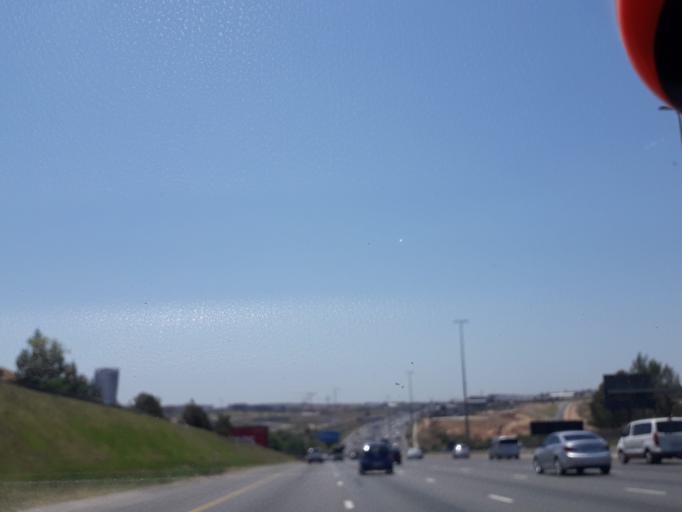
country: ZA
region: Gauteng
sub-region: City of Johannesburg Metropolitan Municipality
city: Midrand
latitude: -26.0346
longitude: 28.1076
